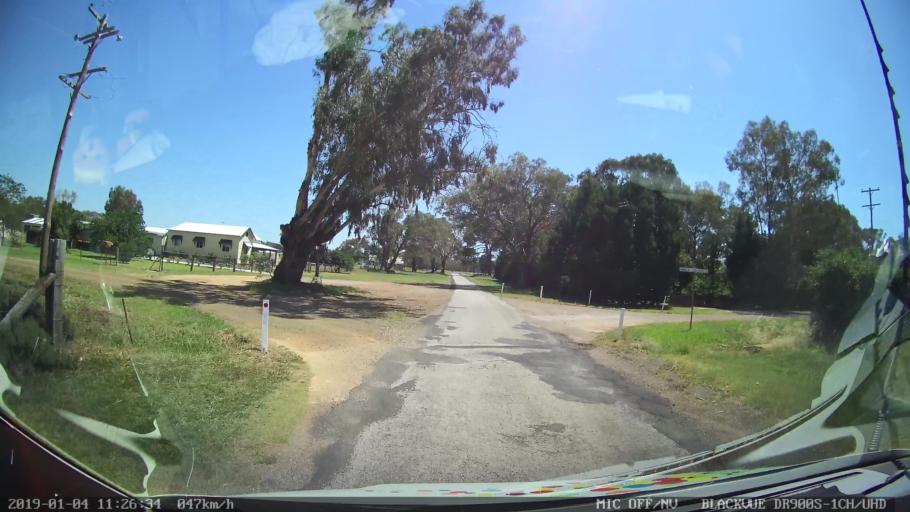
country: AU
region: New South Wales
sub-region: Cabonne
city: Molong
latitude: -33.1144
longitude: 148.7565
